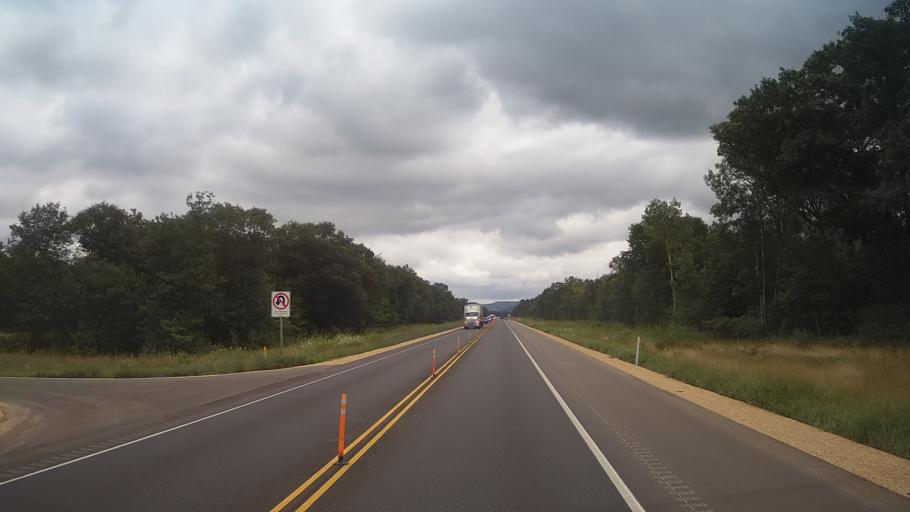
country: US
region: Wisconsin
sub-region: Monroe County
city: Sparta
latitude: 43.9430
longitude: -90.7052
